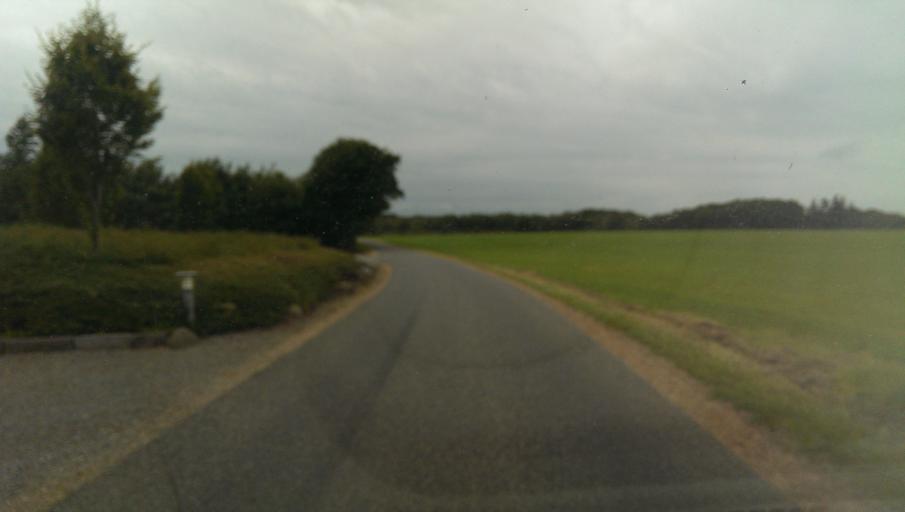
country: DK
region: South Denmark
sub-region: Esbjerg Kommune
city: Bramming
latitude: 55.4761
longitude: 8.7267
